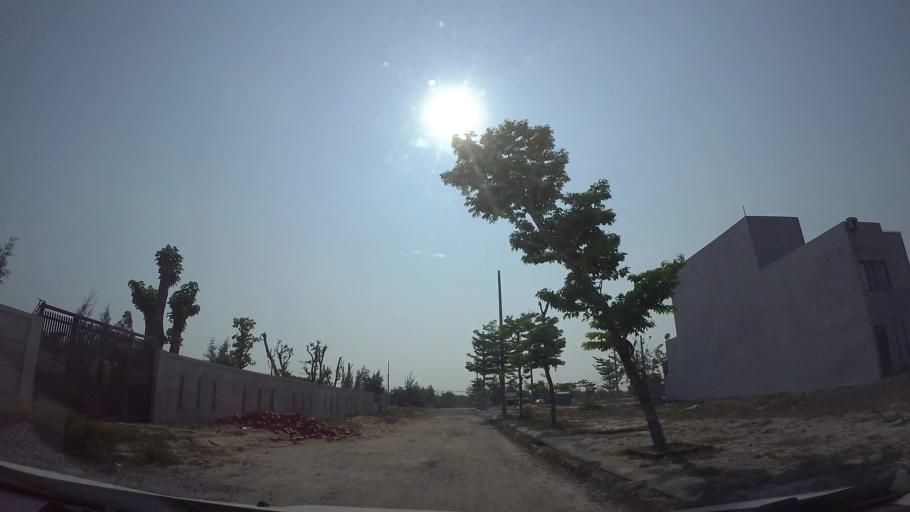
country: VN
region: Da Nang
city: Ngu Hanh Son
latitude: 15.9531
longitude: 108.2758
